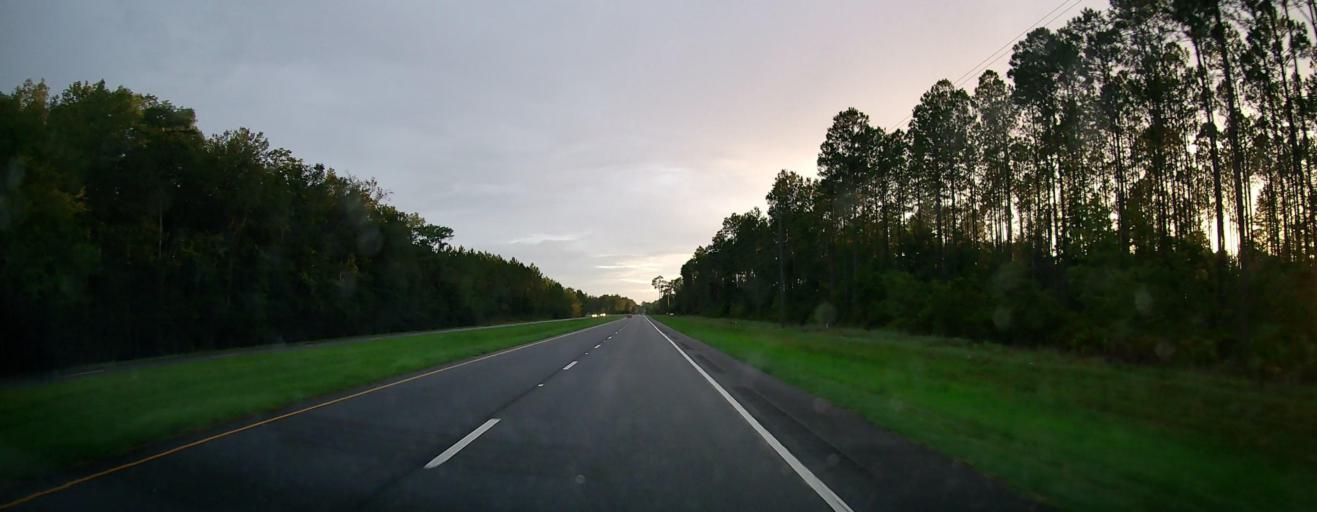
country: US
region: Georgia
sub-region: Clinch County
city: Homerville
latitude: 31.0041
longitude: -82.8578
